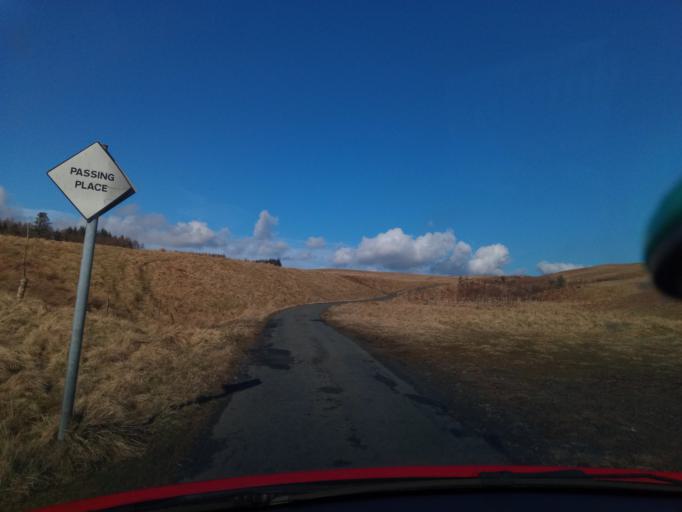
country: GB
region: Scotland
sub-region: The Scottish Borders
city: Hawick
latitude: 55.4308
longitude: -2.8767
